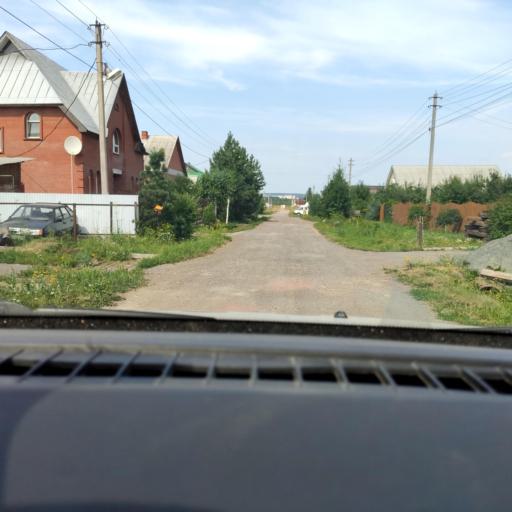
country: RU
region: Perm
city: Froly
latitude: 57.8896
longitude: 56.2522
